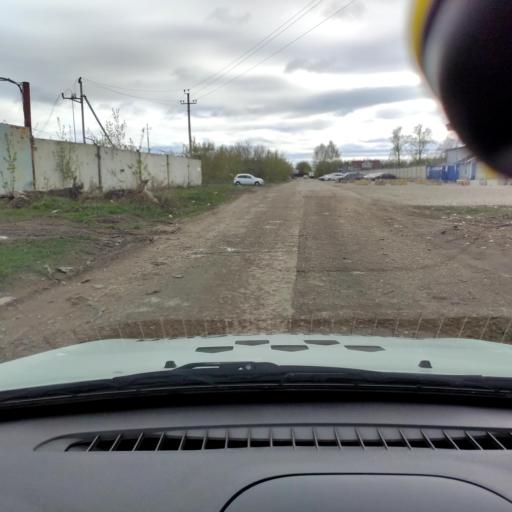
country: RU
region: Samara
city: Tol'yatti
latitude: 53.5792
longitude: 49.3136
